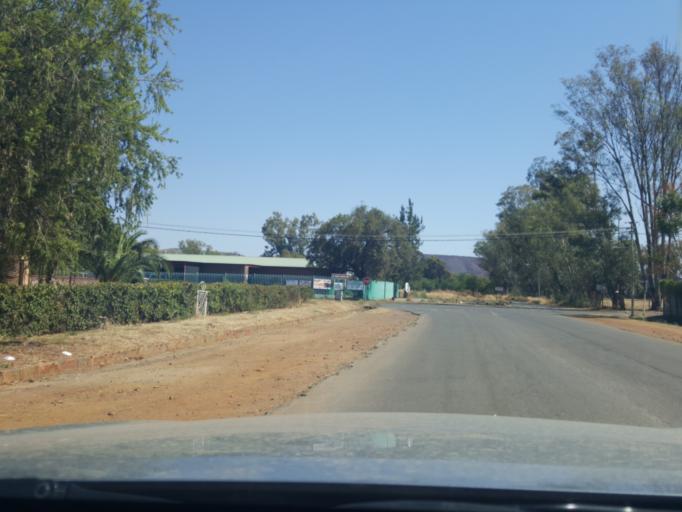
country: ZA
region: North-West
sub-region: Ngaka Modiri Molema District Municipality
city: Zeerust
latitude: -25.5430
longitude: 26.0738
